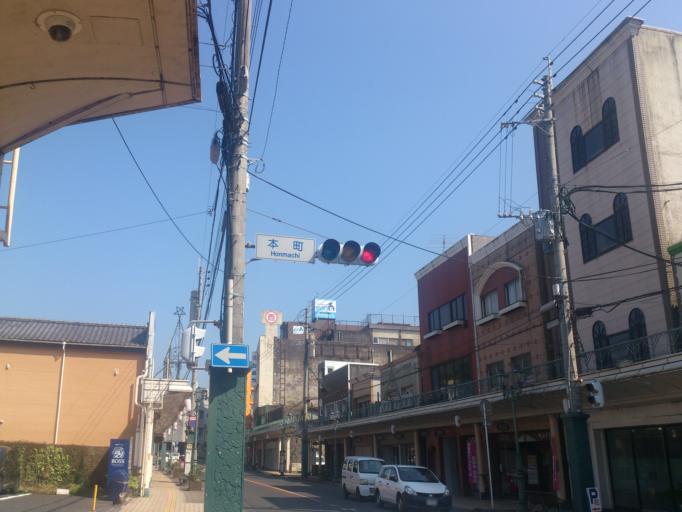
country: JP
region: Kagoshima
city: Kanoya
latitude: 31.3868
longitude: 130.8517
